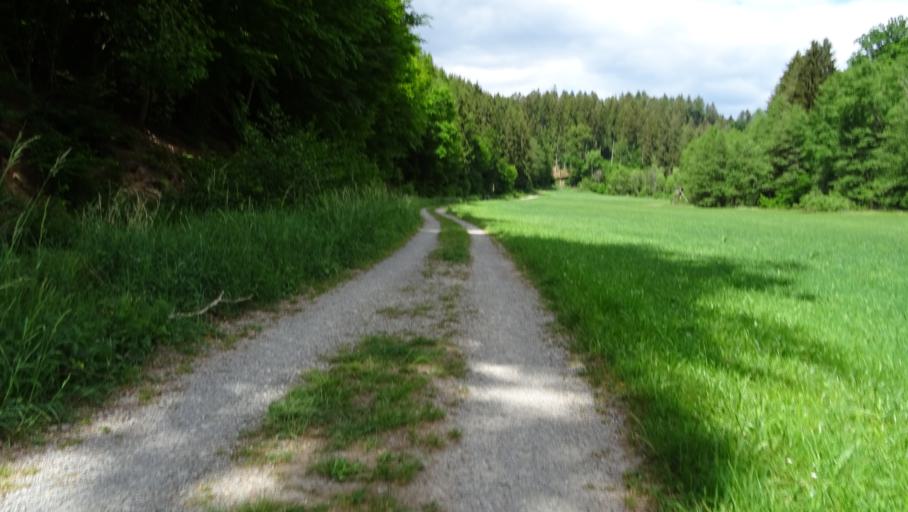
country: DE
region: Baden-Wuerttemberg
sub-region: Karlsruhe Region
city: Fahrenbach
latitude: 49.3997
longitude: 9.1777
